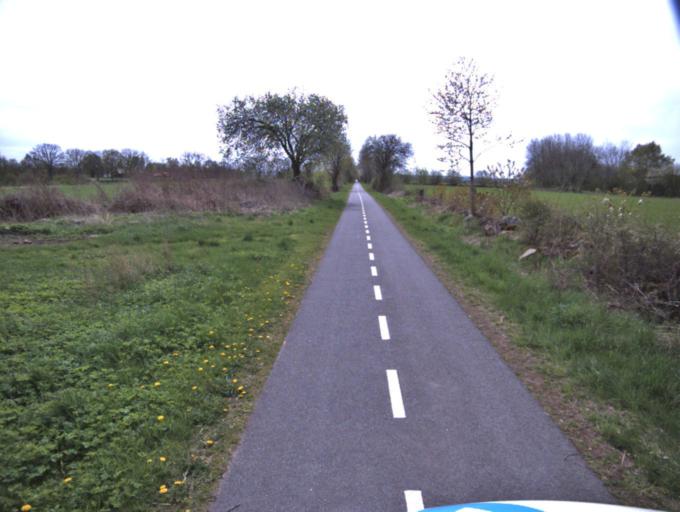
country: SE
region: Skane
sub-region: Kristianstads Kommun
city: Onnestad
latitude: 55.9888
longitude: 14.0314
